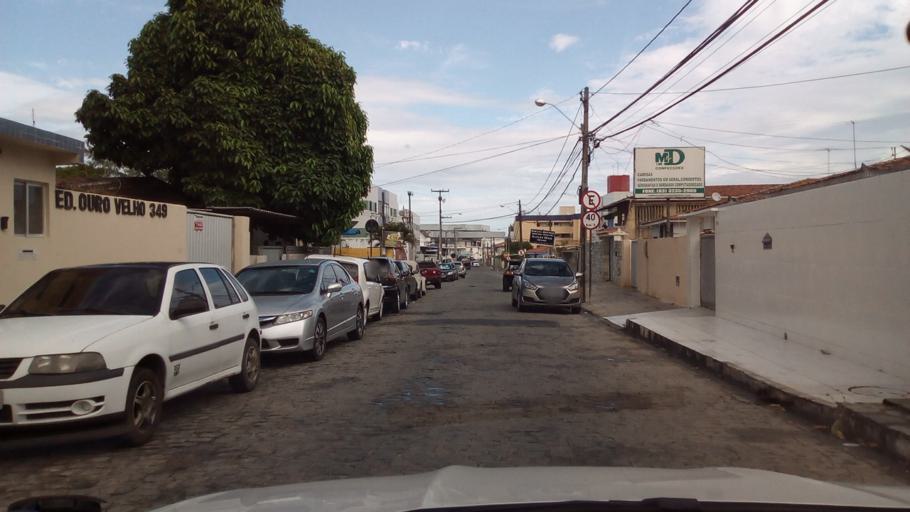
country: BR
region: Paraiba
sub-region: Joao Pessoa
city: Joao Pessoa
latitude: -7.1482
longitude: -34.8457
